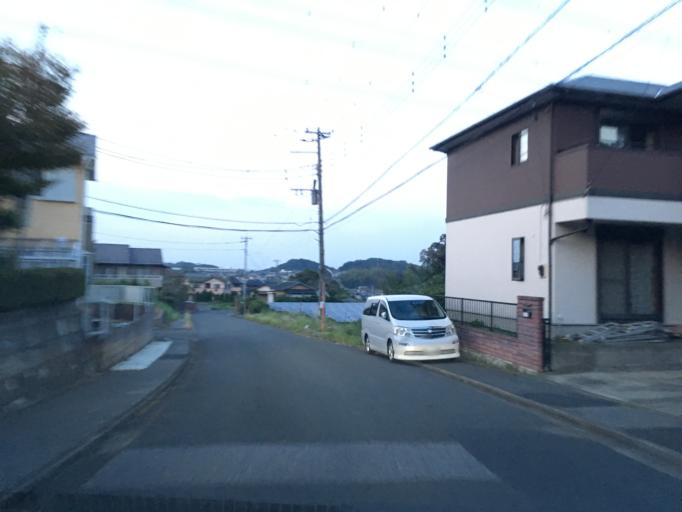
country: JP
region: Chiba
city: Kimitsu
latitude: 35.3397
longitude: 139.9104
